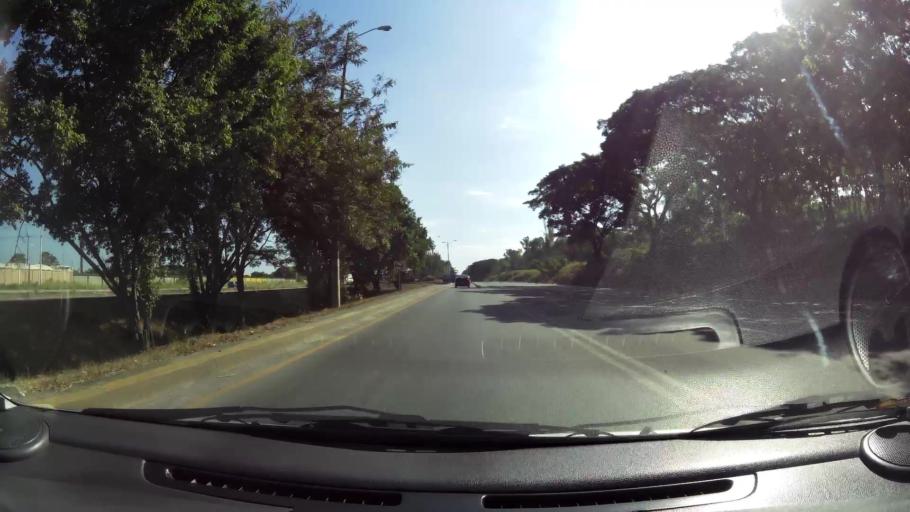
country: EC
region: Guayas
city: Santa Lucia
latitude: -2.1859
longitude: -80.0116
